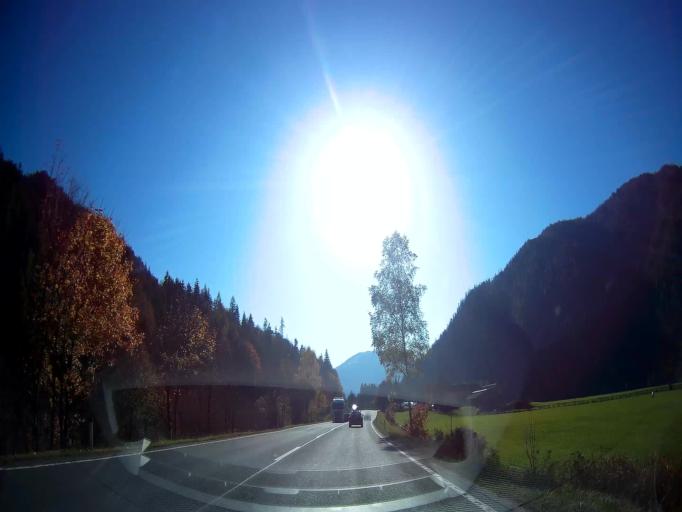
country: AT
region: Salzburg
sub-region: Politischer Bezirk Zell am See
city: Saalfelden am Steinernen Meer
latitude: 47.4723
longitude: 12.8310
